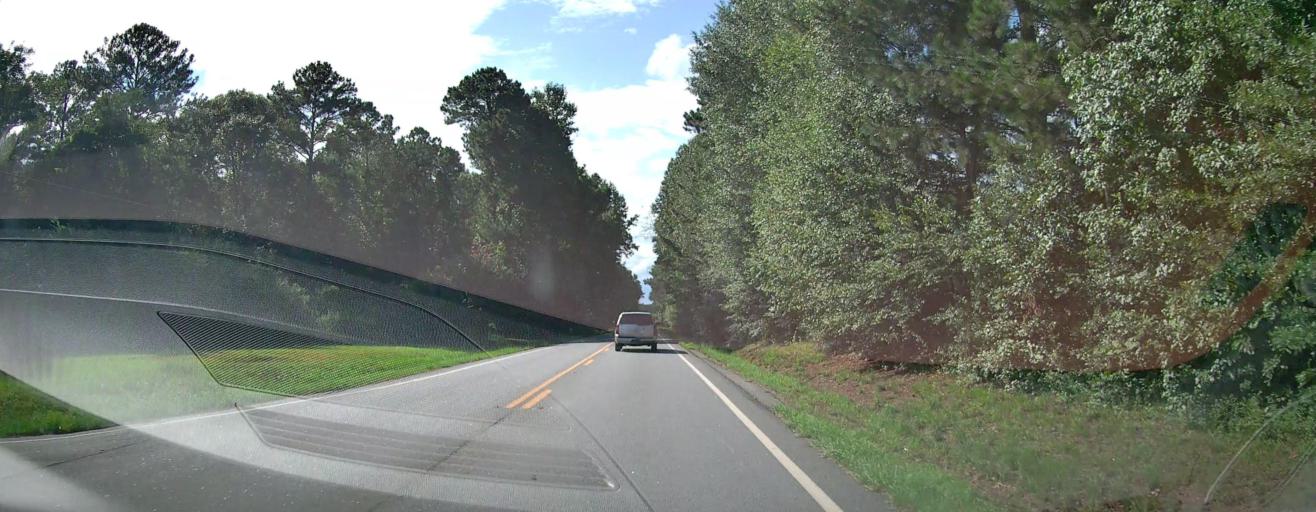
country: US
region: Georgia
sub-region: Upson County
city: Hannahs Mill
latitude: 32.9642
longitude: -84.4727
